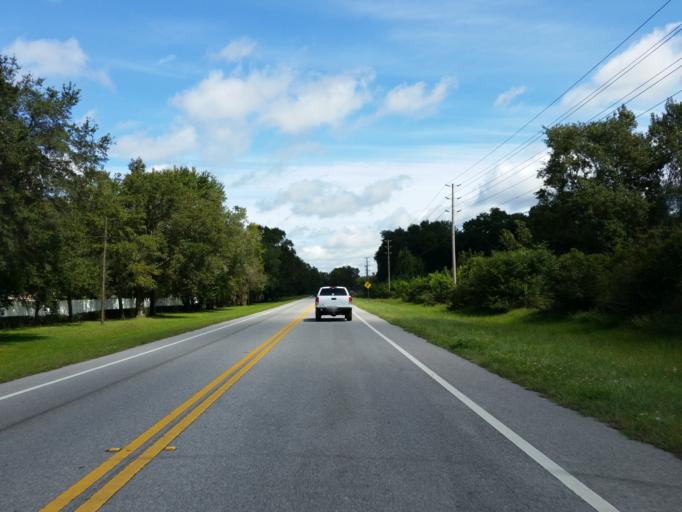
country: US
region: Florida
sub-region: Pasco County
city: Wesley Chapel
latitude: 28.2182
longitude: -82.3876
